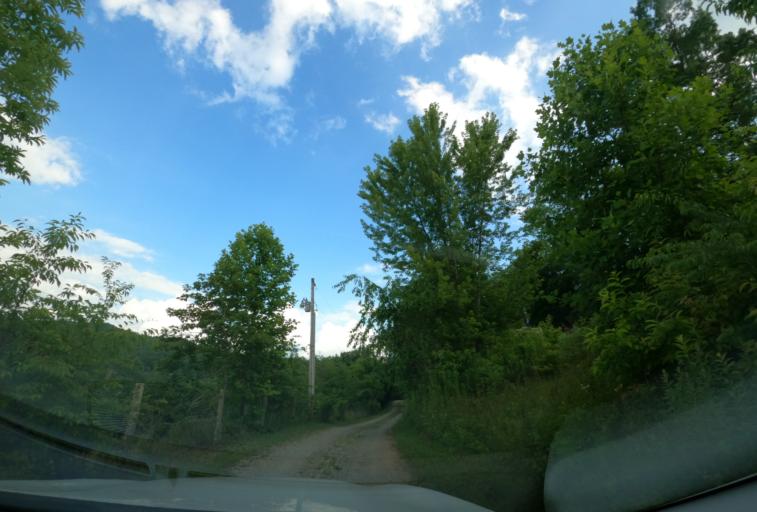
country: US
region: North Carolina
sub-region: Transylvania County
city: Brevard
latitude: 35.2305
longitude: -82.8571
